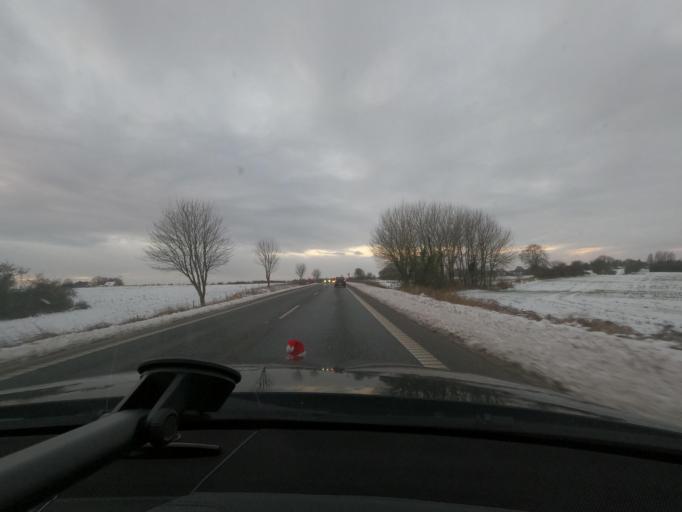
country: DK
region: South Denmark
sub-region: Aabenraa Kommune
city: Krusa
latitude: 54.8752
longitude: 9.4679
